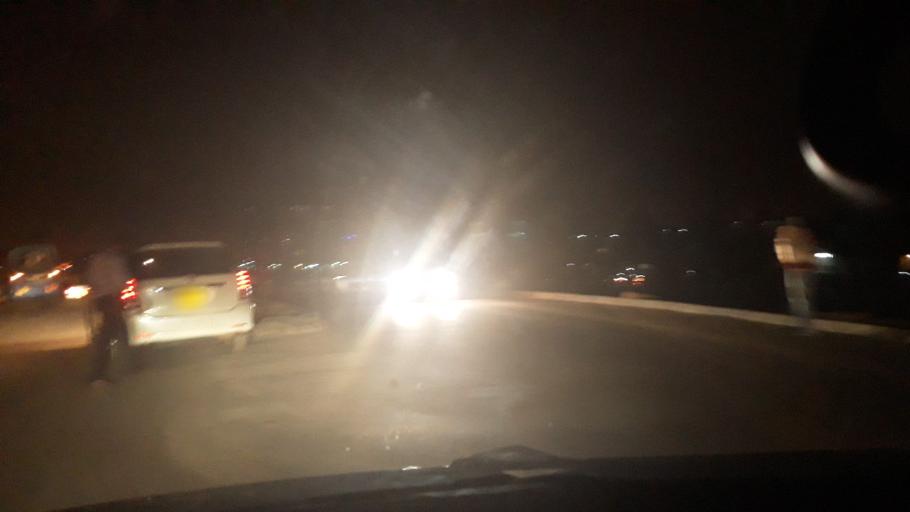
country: KE
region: Nairobi Area
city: Pumwani
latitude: -1.2988
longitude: 36.8863
